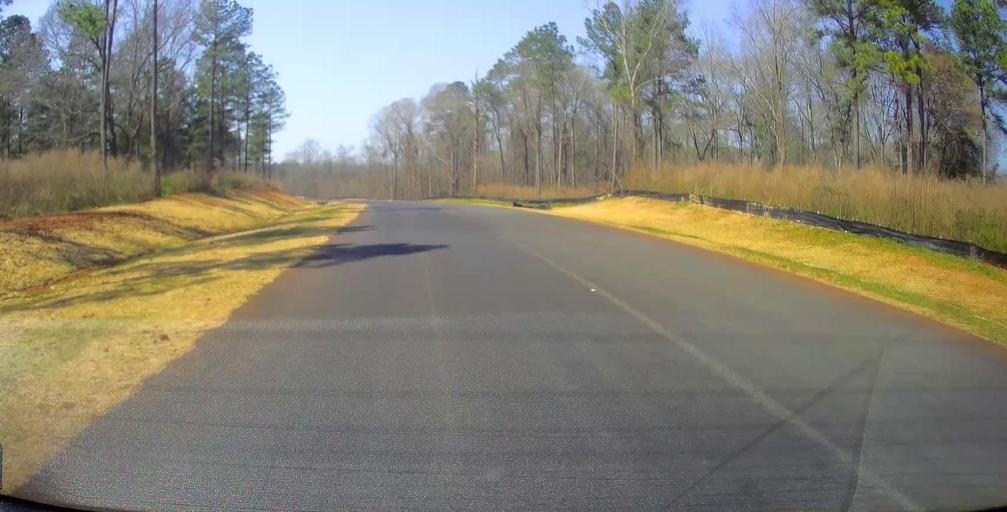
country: US
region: Georgia
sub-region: Houston County
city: Centerville
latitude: 32.6016
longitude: -83.7314
